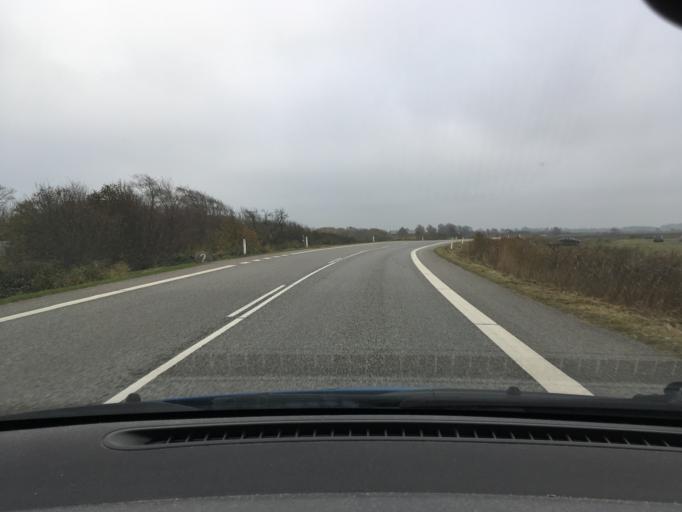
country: DE
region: Schleswig-Holstein
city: Aventoft
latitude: 54.9181
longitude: 8.8333
